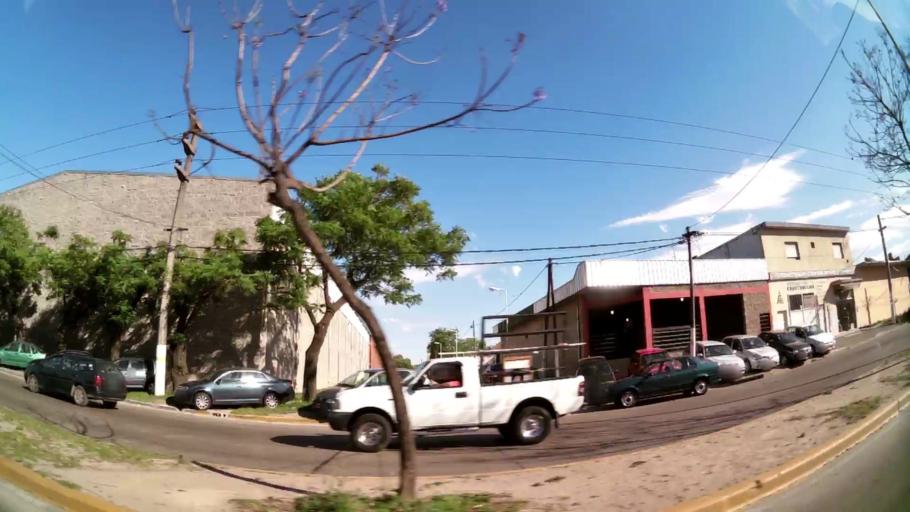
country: AR
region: Buenos Aires
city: Santa Catalina - Dique Lujan
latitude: -34.4796
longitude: -58.6753
